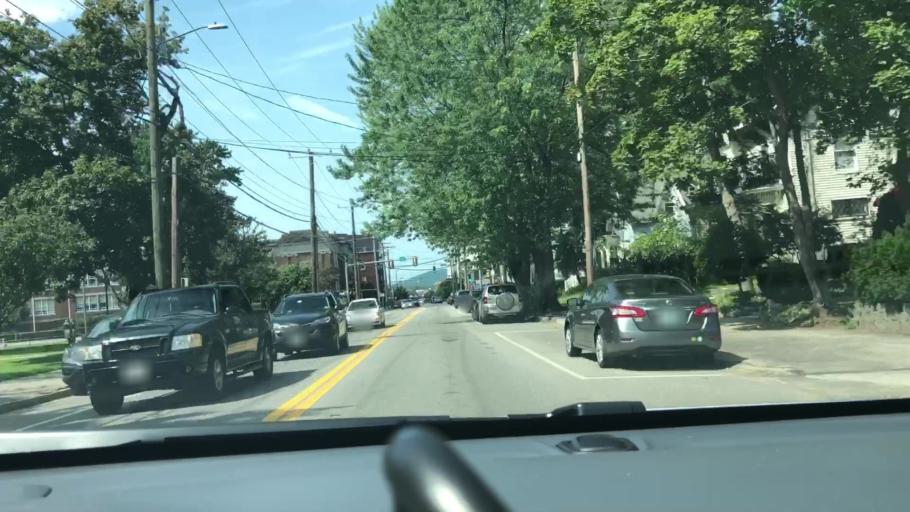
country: US
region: New Hampshire
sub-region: Hillsborough County
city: Manchester
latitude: 42.9952
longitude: -71.4583
